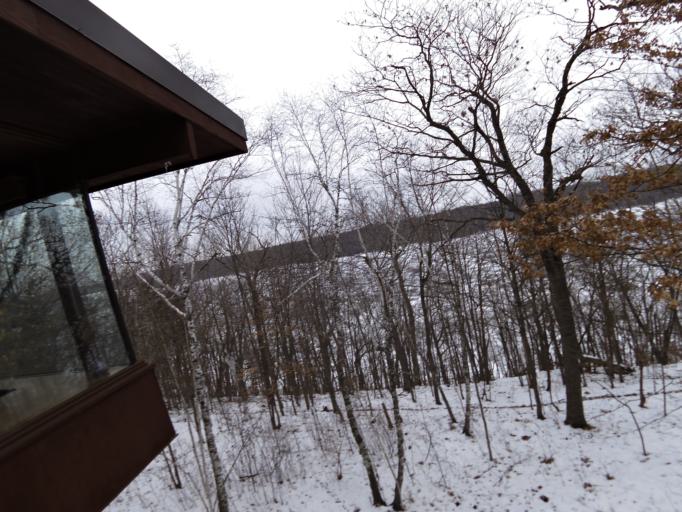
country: US
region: Wisconsin
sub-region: Pierce County
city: Prescott
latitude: 44.8034
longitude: -92.7875
